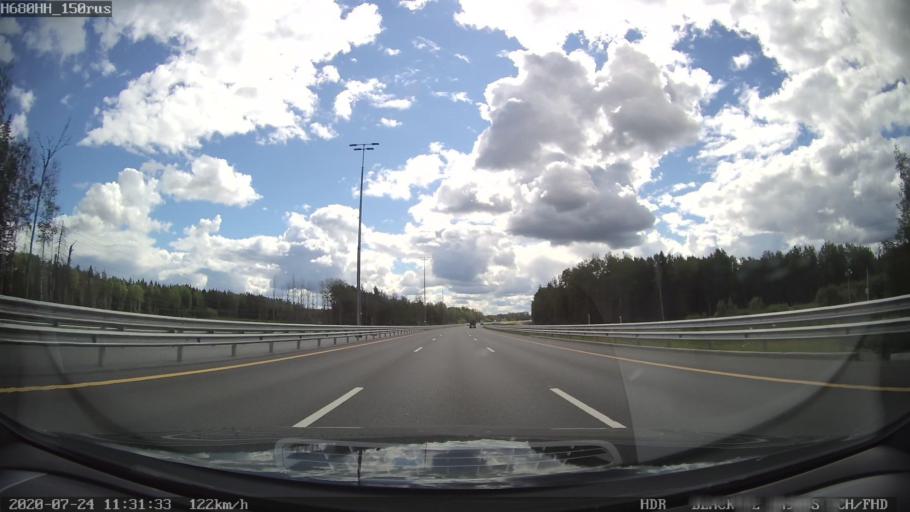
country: RU
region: Leningrad
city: Krasnyy Bor
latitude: 59.6547
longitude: 30.6405
